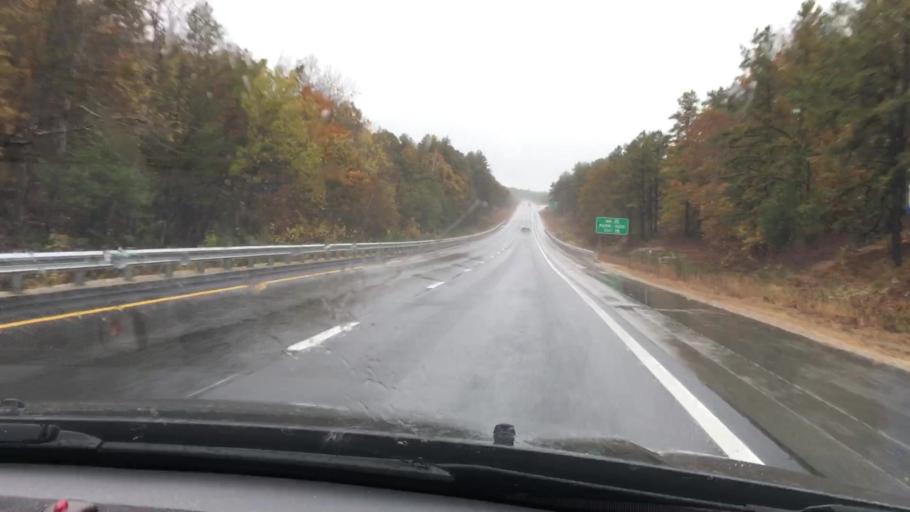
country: US
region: New Hampshire
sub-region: Merrimack County
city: Boscawen
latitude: 43.3368
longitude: -71.6140
